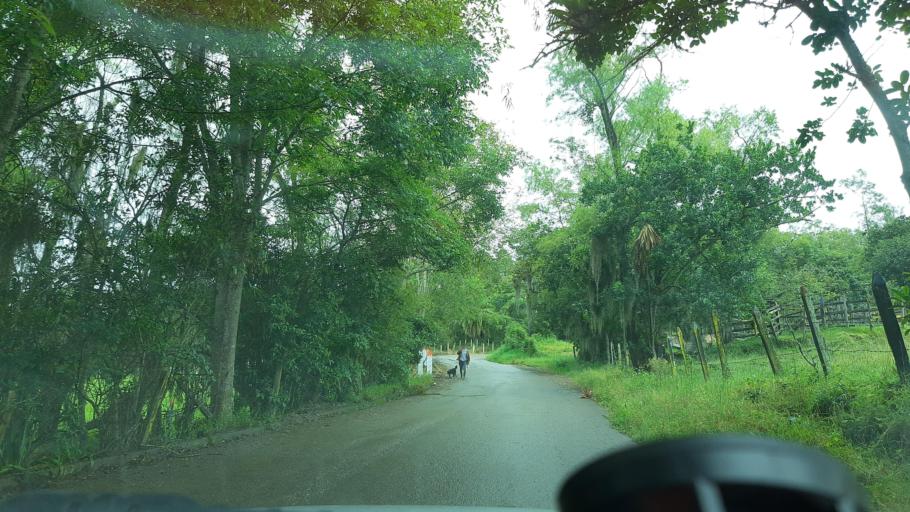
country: CO
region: Cundinamarca
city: Manta
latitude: 5.0525
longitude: -73.5093
